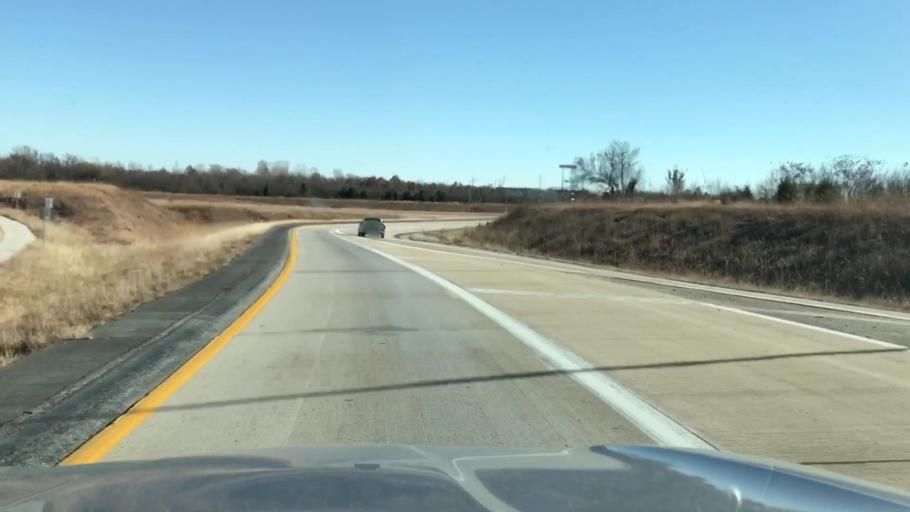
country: US
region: Missouri
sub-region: Jasper County
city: Duenweg
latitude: 37.0592
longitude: -94.4290
